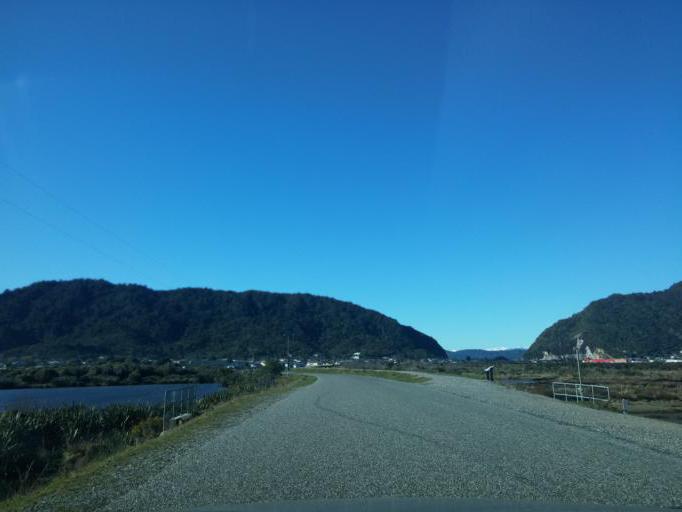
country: NZ
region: West Coast
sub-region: Grey District
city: Greymouth
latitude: -42.4405
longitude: 171.1995
